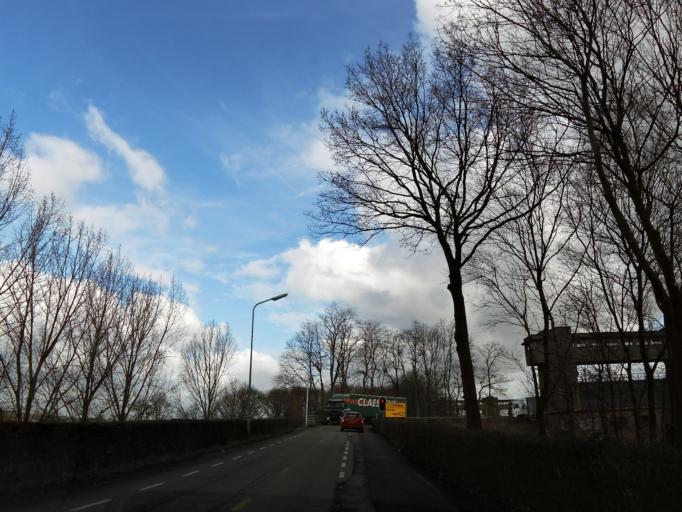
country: NL
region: Limburg
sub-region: Gemeente Maastricht
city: Maastricht
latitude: 50.8735
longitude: 5.7002
